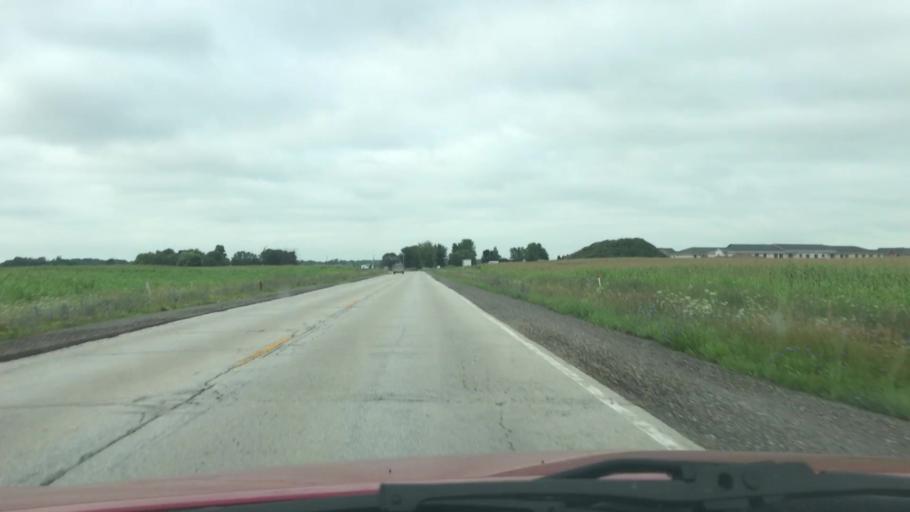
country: US
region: Wisconsin
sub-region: Brown County
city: De Pere
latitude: 44.4422
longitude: -88.1340
